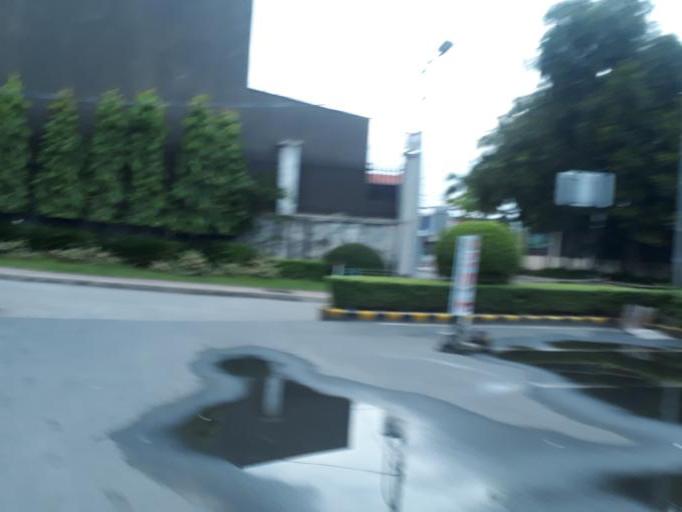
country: PH
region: Calabarzon
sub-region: Province of Rizal
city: Valenzuela
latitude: 14.7088
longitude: 120.9575
